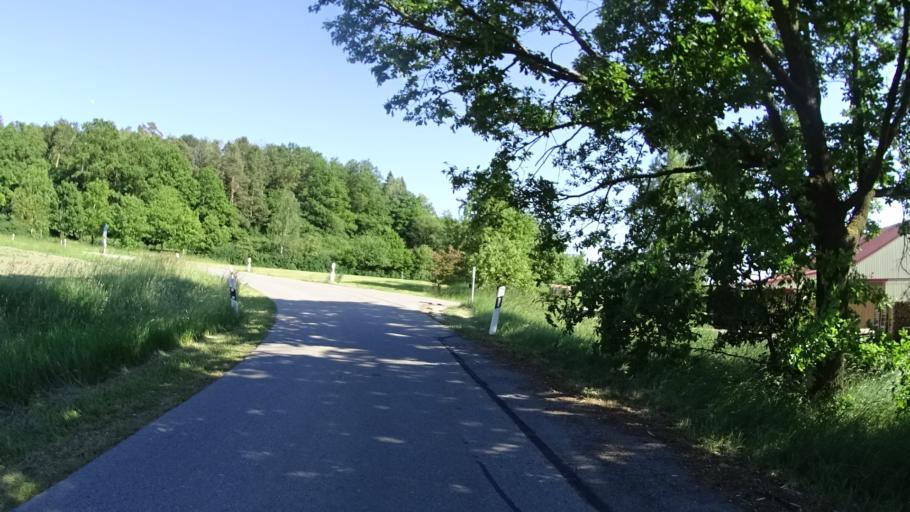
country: DE
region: Bavaria
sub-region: Regierungsbezirk Mittelfranken
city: Feuchtwangen
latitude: 49.1778
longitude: 10.3246
